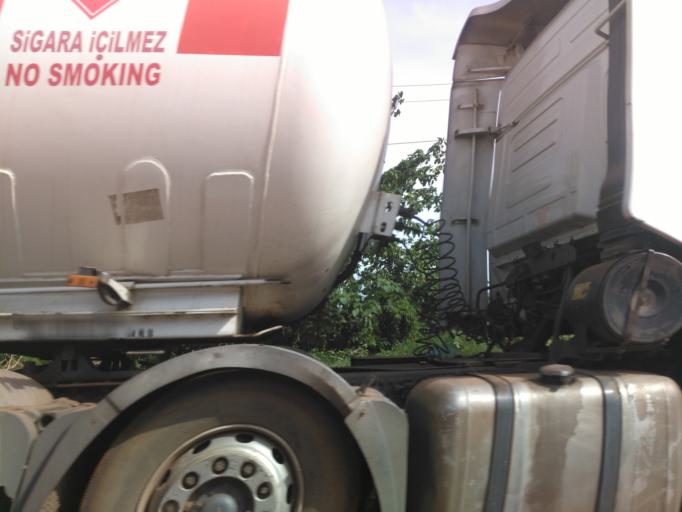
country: UG
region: Eastern Region
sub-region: Jinja District
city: Jinja
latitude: 0.4266
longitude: 33.2185
